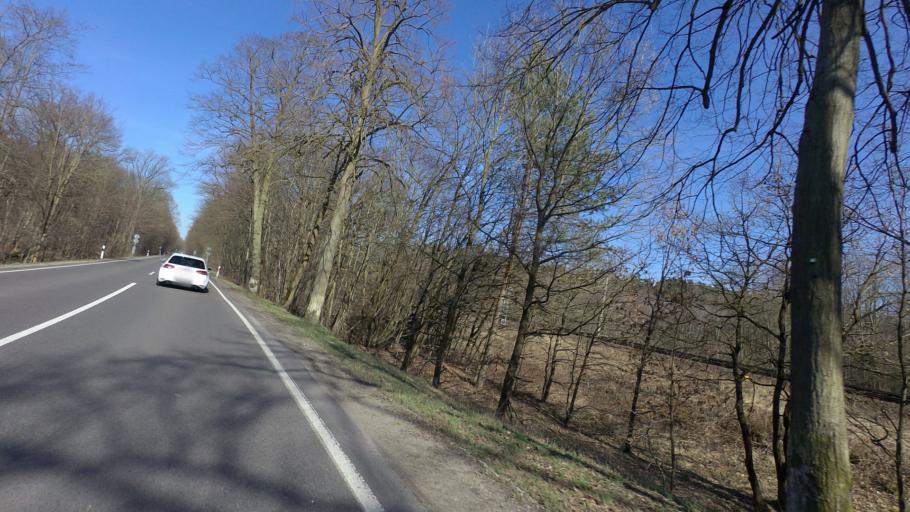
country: DE
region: Brandenburg
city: Chorin
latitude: 52.9201
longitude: 13.9067
